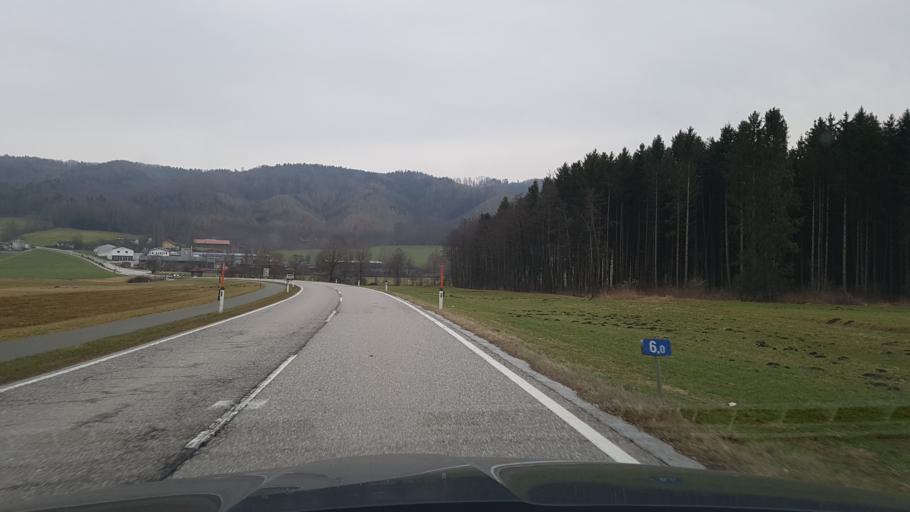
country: AT
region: Salzburg
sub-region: Politischer Bezirk Salzburg-Umgebung
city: Dorfbeuern
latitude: 48.0056
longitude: 13.0296
